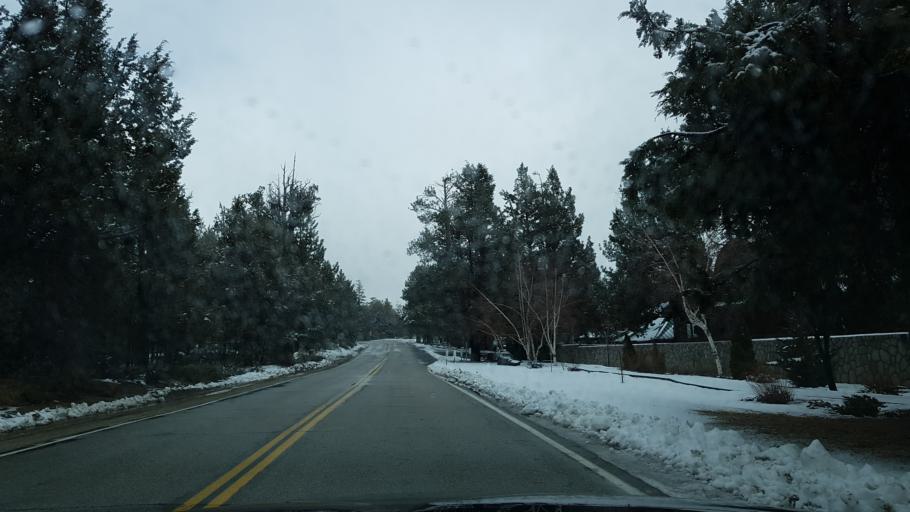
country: US
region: California
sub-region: San Bernardino County
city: Big Bear Lake
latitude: 34.2620
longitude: -116.9135
